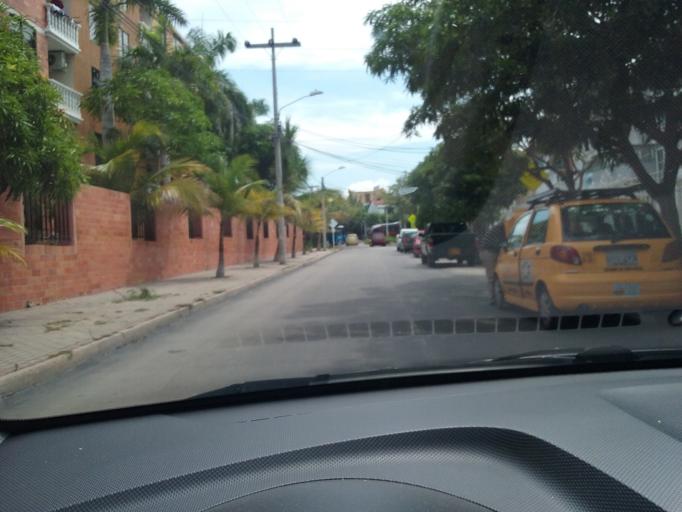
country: CO
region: Atlantico
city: Barranquilla
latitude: 11.0199
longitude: -74.8140
